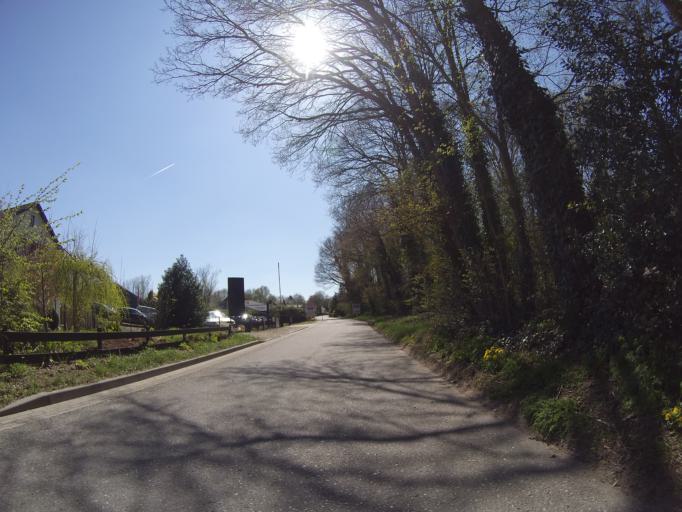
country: NL
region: Utrecht
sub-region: Gemeente Rhenen
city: Rhenen
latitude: 51.9645
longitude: 5.5816
